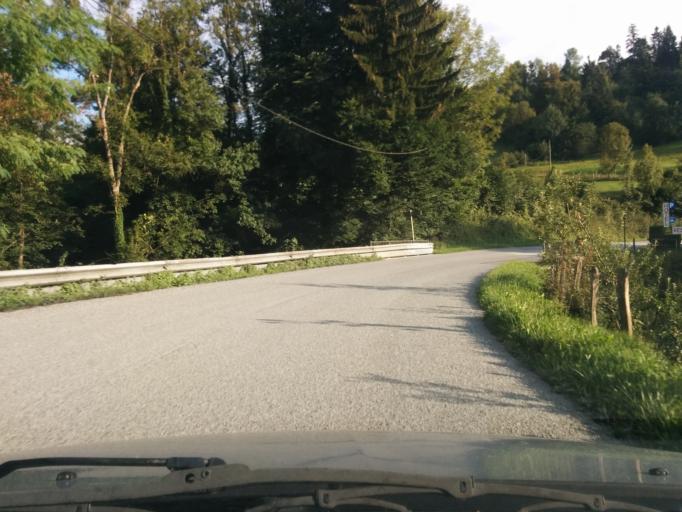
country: FR
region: Rhone-Alpes
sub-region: Departement de la Savoie
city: Saint-Beron
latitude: 45.4726
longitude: 5.7388
